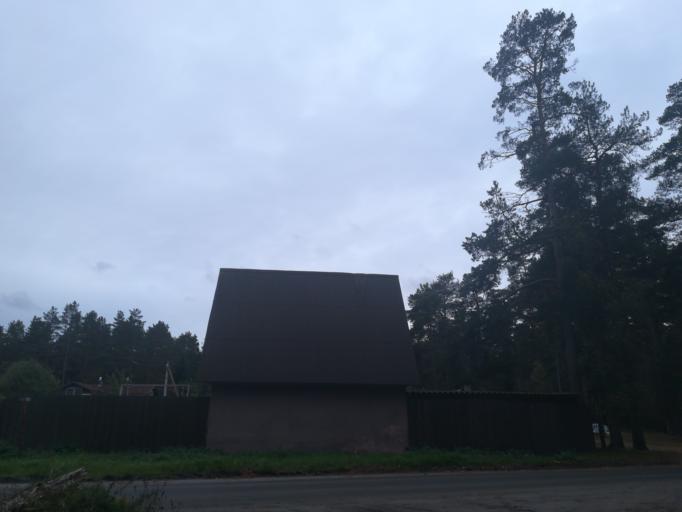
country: RU
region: Leningrad
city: Priozersk
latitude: 61.0387
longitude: 30.1880
